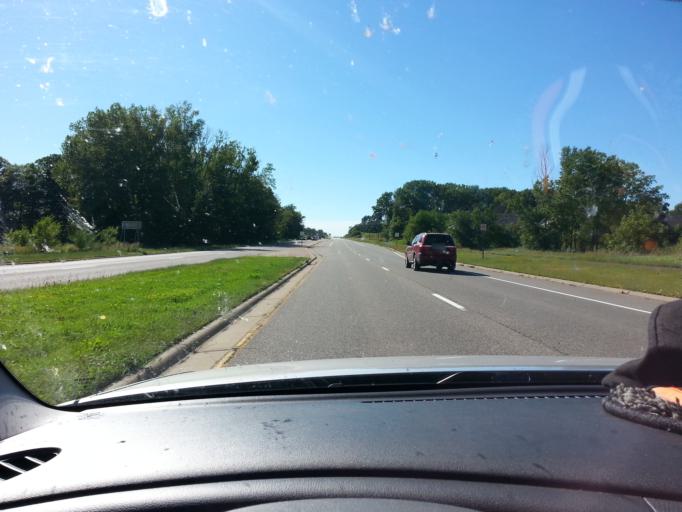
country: US
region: Minnesota
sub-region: Dakota County
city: Lakeville
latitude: 44.6814
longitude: -93.3029
